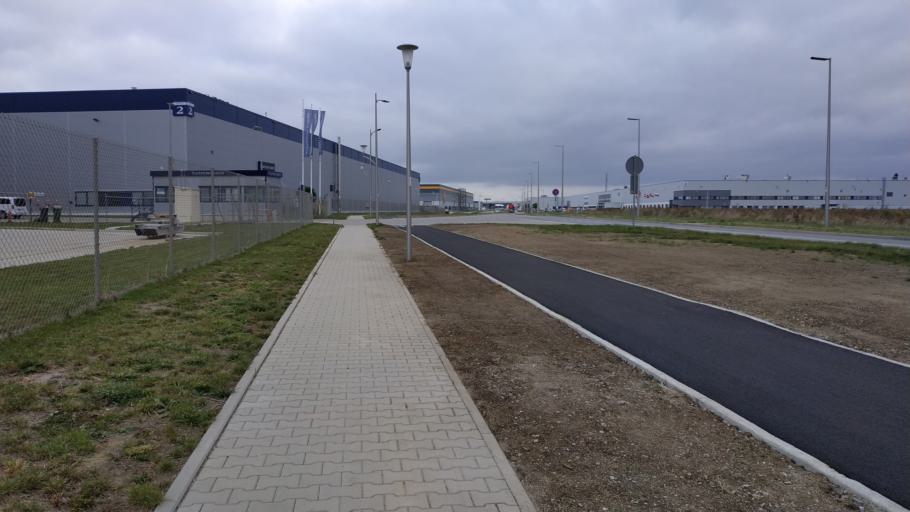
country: PL
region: Lower Silesian Voivodeship
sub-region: Powiat wroclawski
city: Bielany Wroclawskie
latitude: 51.0325
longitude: 16.9500
